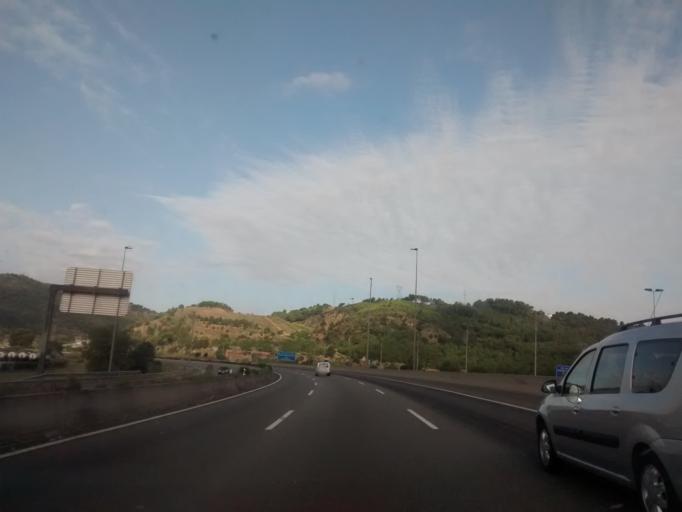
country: ES
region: Catalonia
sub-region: Provincia de Barcelona
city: Castellbisbal
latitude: 41.4715
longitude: 1.9600
